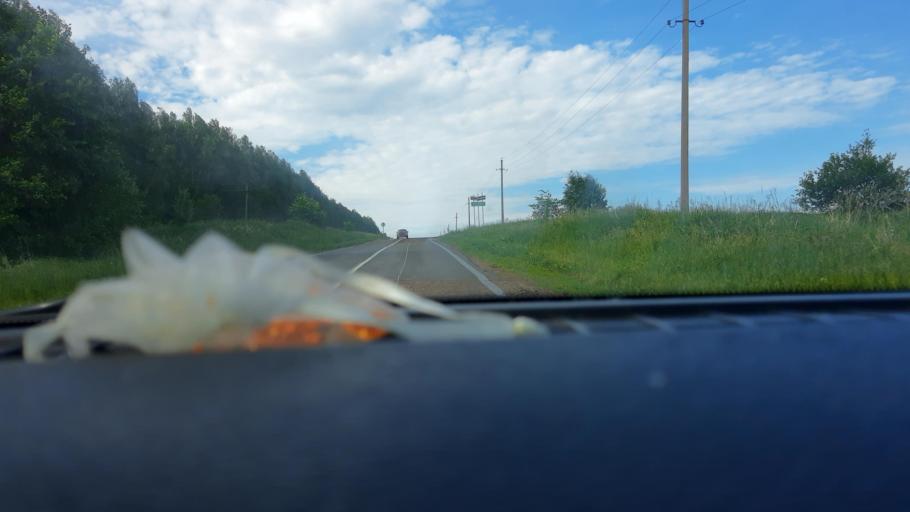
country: RU
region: Bashkortostan
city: Ulukulevo
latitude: 54.5469
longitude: 56.4337
